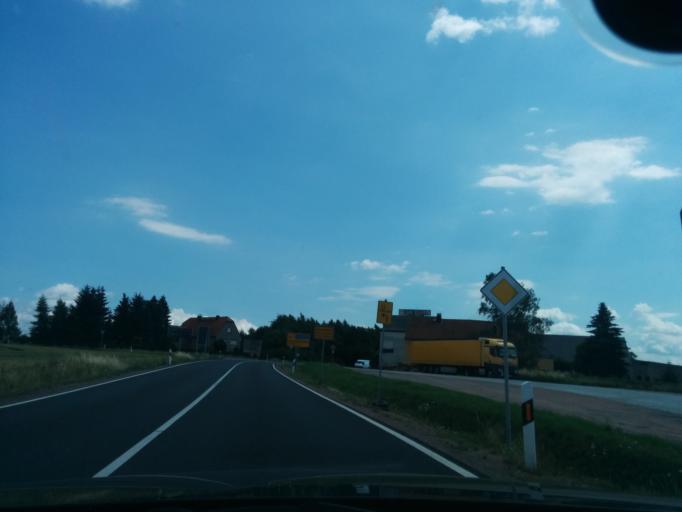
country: DE
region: Saxony
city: Hainichen
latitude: 51.0163
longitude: 13.1256
